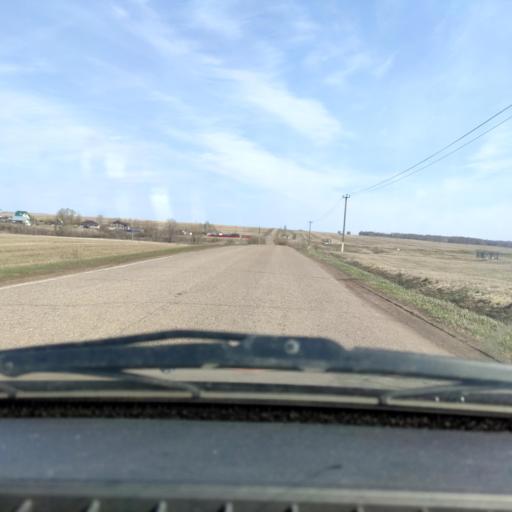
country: RU
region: Bashkortostan
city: Asanovo
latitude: 54.7802
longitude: 55.5012
